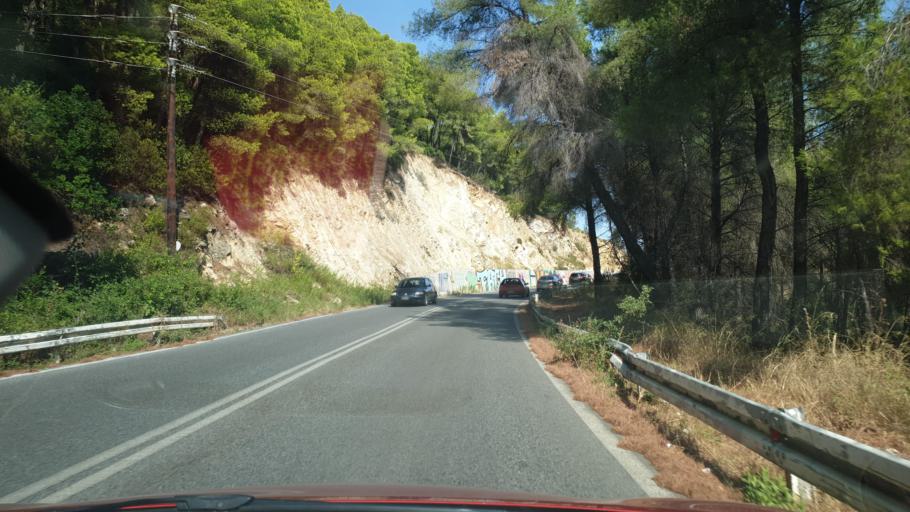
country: GR
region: Central Macedonia
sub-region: Nomos Chalkidikis
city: Agios Nikolaos
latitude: 40.2097
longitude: 23.7574
